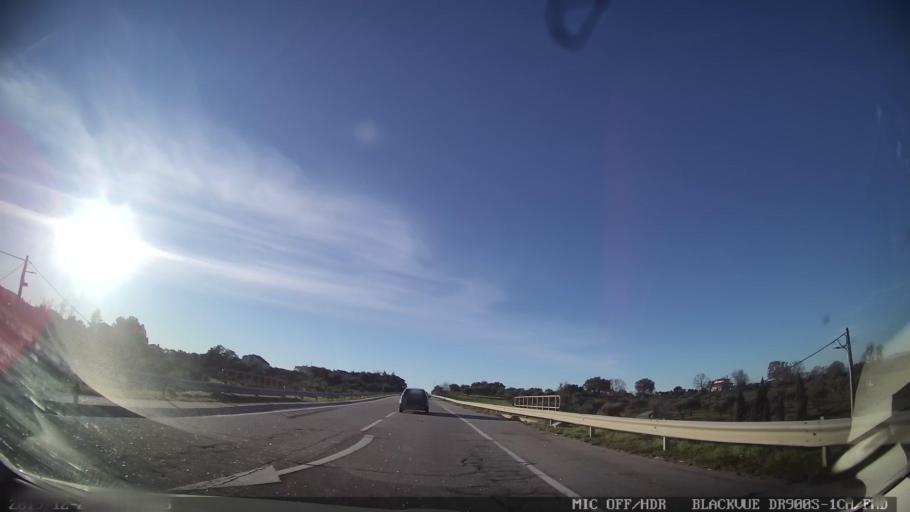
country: PT
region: Castelo Branco
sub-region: Castelo Branco
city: Castelo Branco
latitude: 39.8453
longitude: -7.4874
